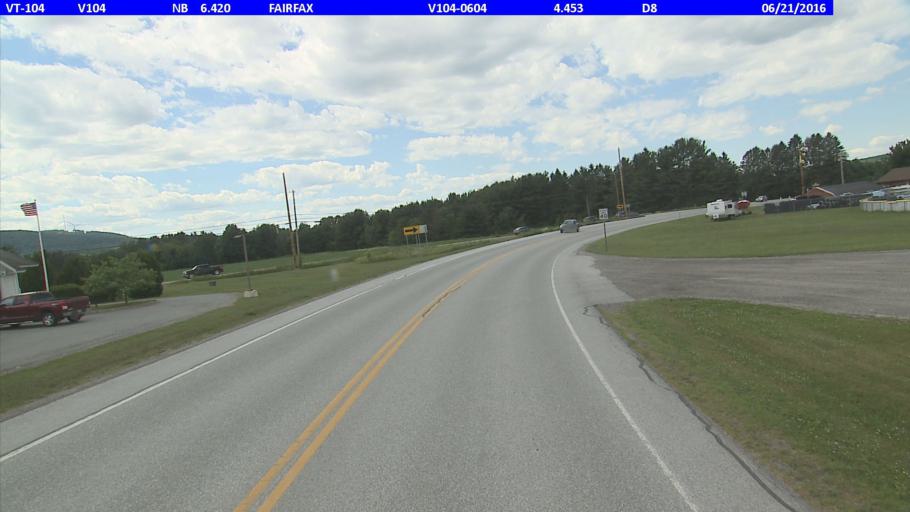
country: US
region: Vermont
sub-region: Chittenden County
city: Milton
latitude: 44.6544
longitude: -73.0085
